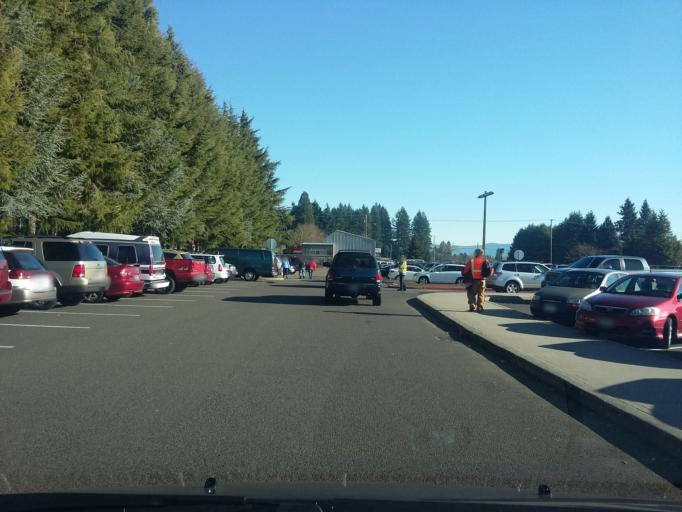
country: US
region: Washington
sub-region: Clark County
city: Brush Prairie
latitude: 45.7061
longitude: -122.5556
